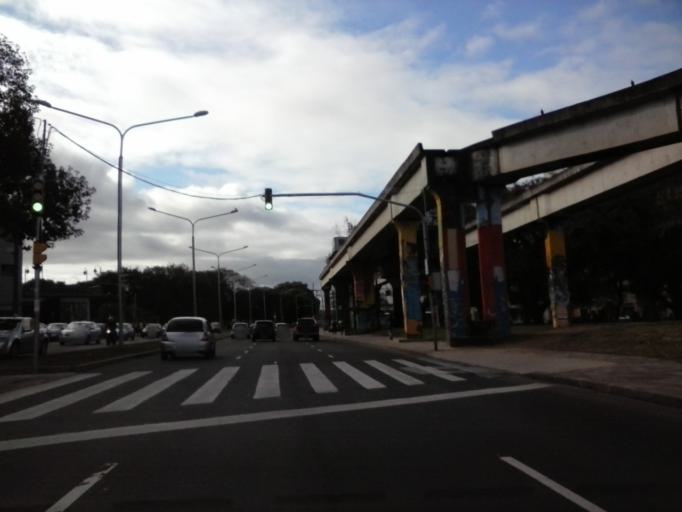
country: BR
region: Rio Grande do Sul
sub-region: Porto Alegre
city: Porto Alegre
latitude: -30.0348
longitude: -51.2406
